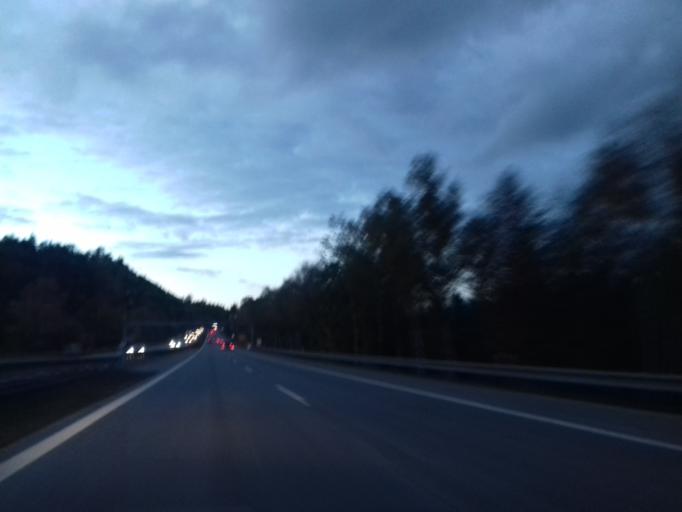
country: CZ
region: Central Bohemia
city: Divisov
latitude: 49.7821
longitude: 14.9317
